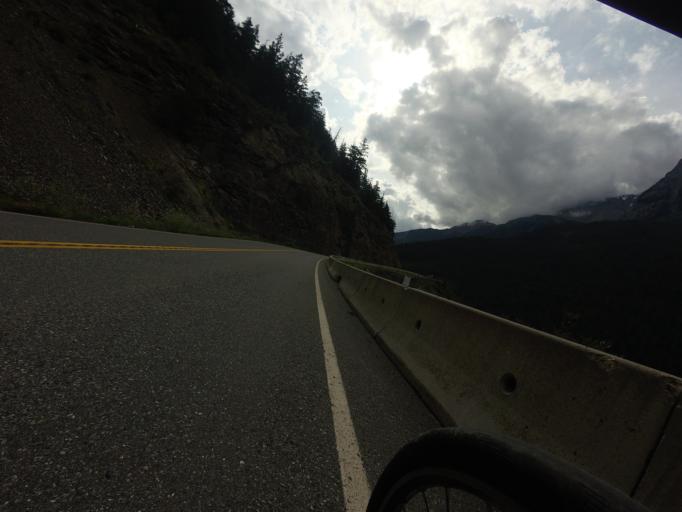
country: CA
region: British Columbia
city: Lillooet
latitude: 50.6427
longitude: -122.0319
